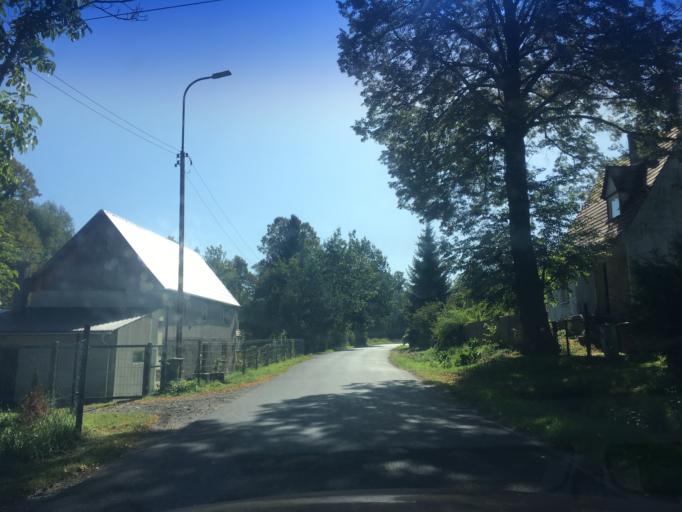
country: PL
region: Lower Silesian Voivodeship
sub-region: Powiat lubanski
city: Siekierczyn
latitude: 51.0591
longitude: 15.1720
